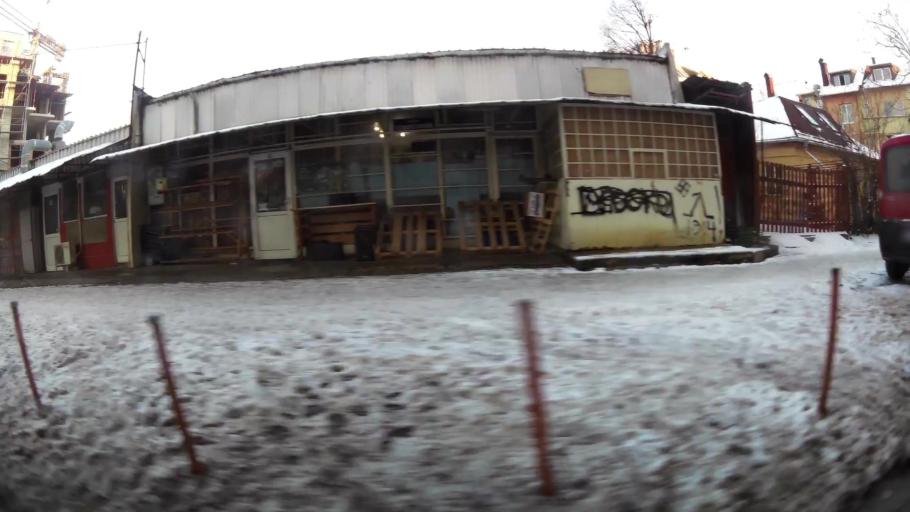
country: BG
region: Sofia-Capital
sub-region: Stolichna Obshtina
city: Sofia
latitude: 42.6904
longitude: 23.3639
